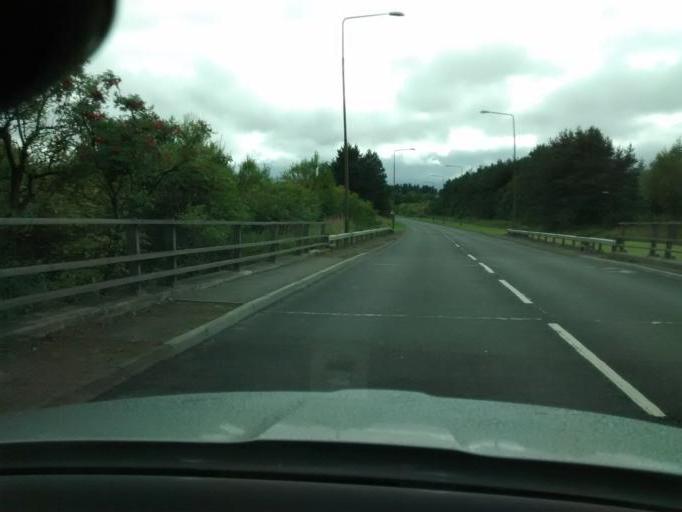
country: GB
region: Scotland
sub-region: West Lothian
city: West Calder
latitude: 55.8933
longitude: -3.5678
